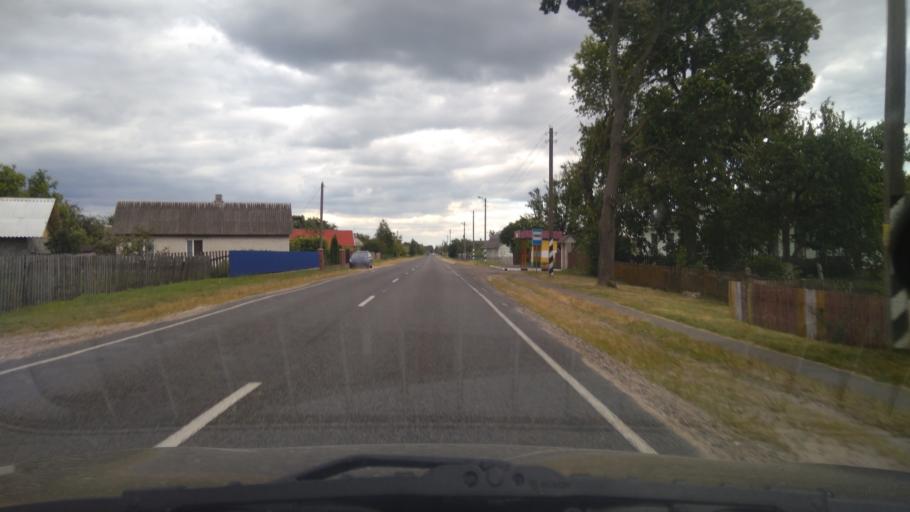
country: BY
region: Brest
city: Byelaazyorsk
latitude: 52.5080
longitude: 25.1684
